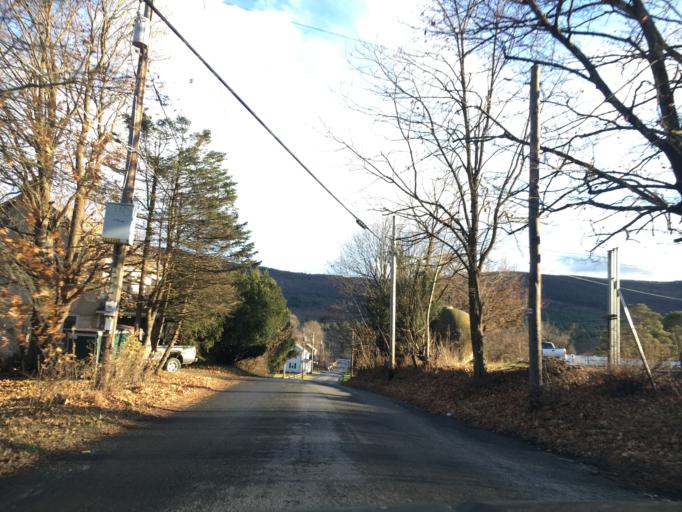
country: US
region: Pennsylvania
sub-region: Carbon County
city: Lehighton
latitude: 40.7844
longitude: -75.7134
